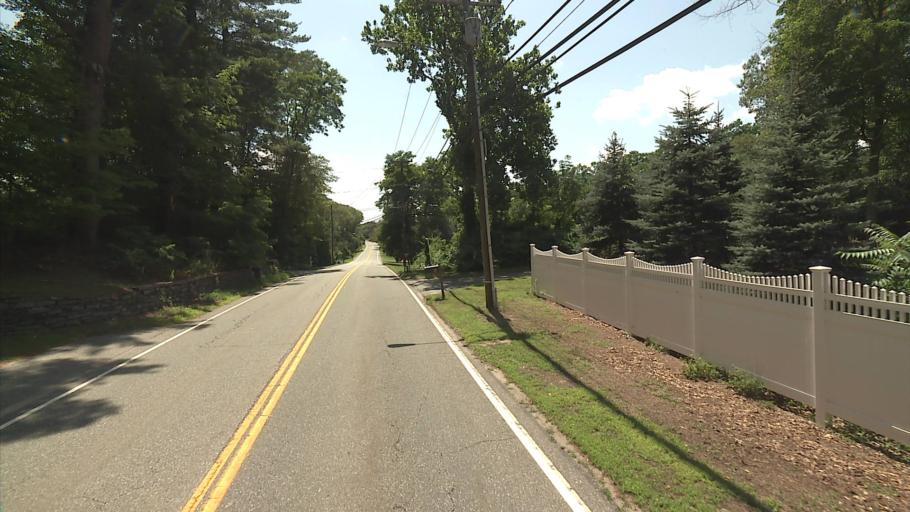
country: US
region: Connecticut
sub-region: Middlesex County
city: Chester Center
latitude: 41.4082
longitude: -72.4403
